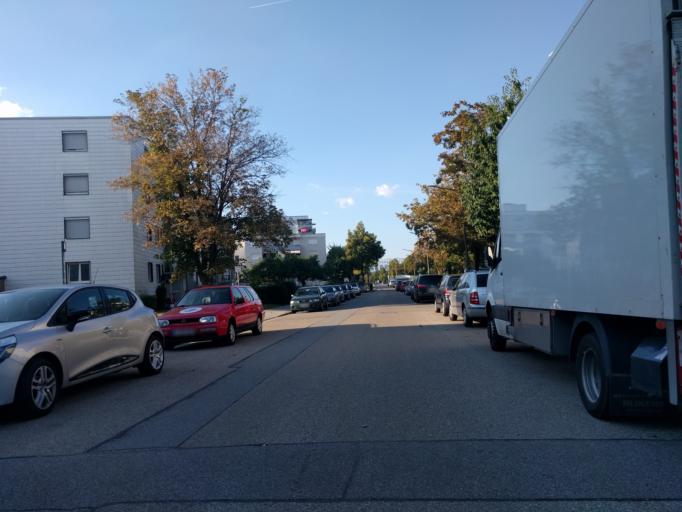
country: DE
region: Bavaria
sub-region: Upper Palatinate
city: Regensburg
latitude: 49.0243
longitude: 12.1223
